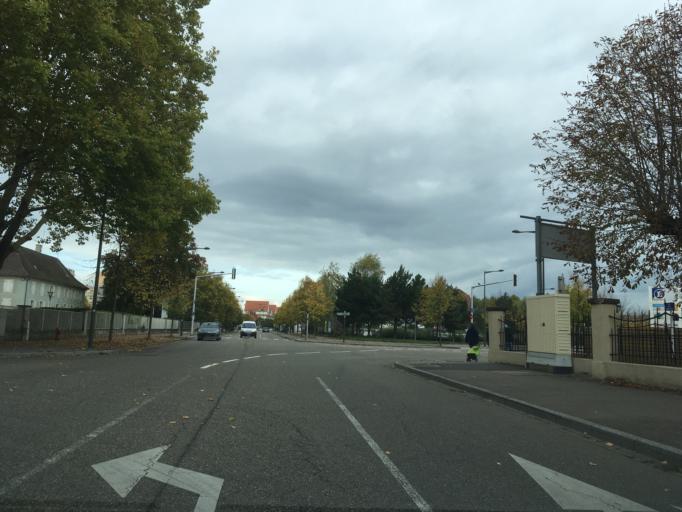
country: FR
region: Alsace
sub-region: Departement du Bas-Rhin
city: Strasbourg
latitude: 48.5441
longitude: 7.7658
